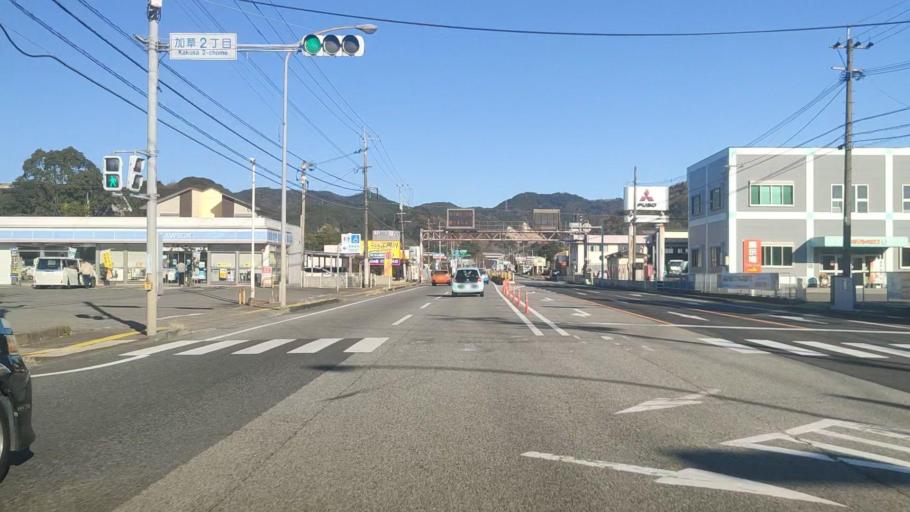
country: JP
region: Miyazaki
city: Nobeoka
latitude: 32.4914
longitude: 131.6636
